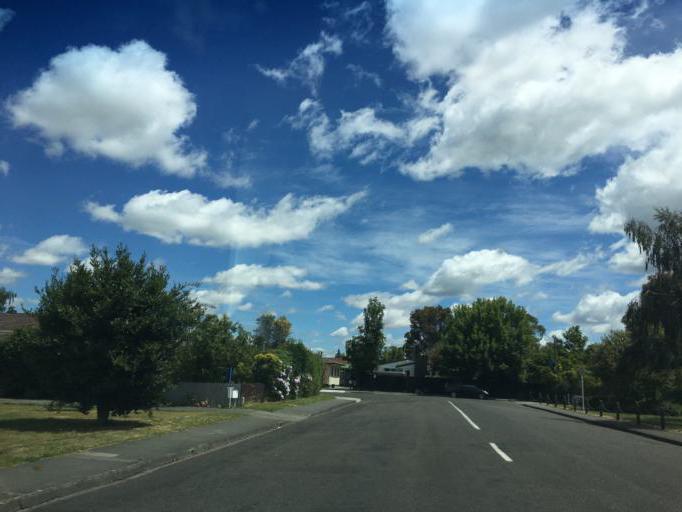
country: NZ
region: Hawke's Bay
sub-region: Hastings District
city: Hastings
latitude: -39.6468
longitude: 176.8602
